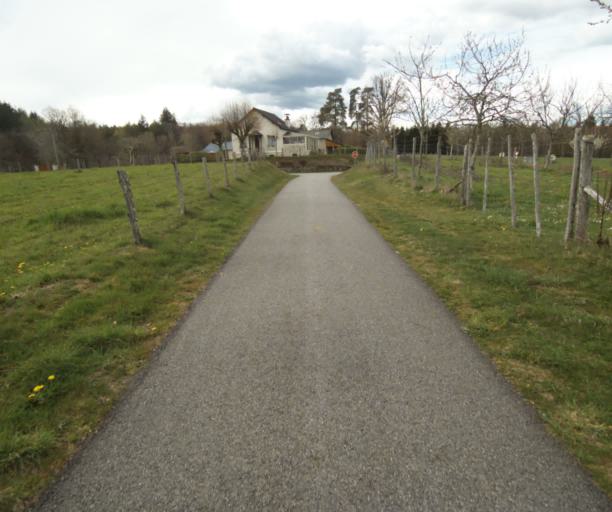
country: FR
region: Limousin
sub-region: Departement de la Correze
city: Argentat
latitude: 45.2163
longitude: 1.9598
